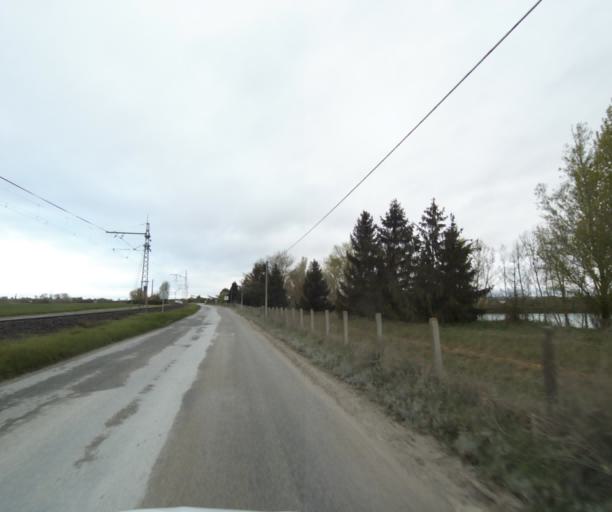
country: FR
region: Midi-Pyrenees
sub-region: Departement de l'Ariege
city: Saverdun
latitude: 43.2261
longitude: 1.6097
